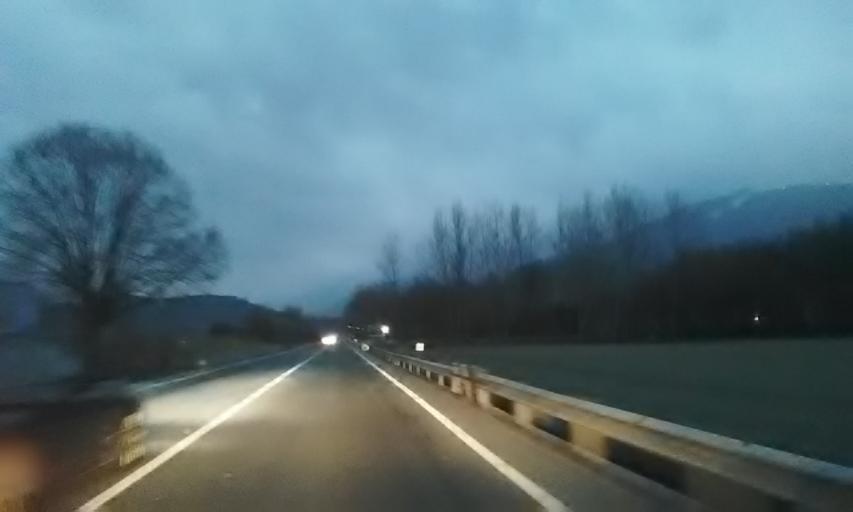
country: IT
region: Piedmont
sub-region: Provincia di Torino
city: Montalto Dora
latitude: 45.5008
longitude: 7.8575
